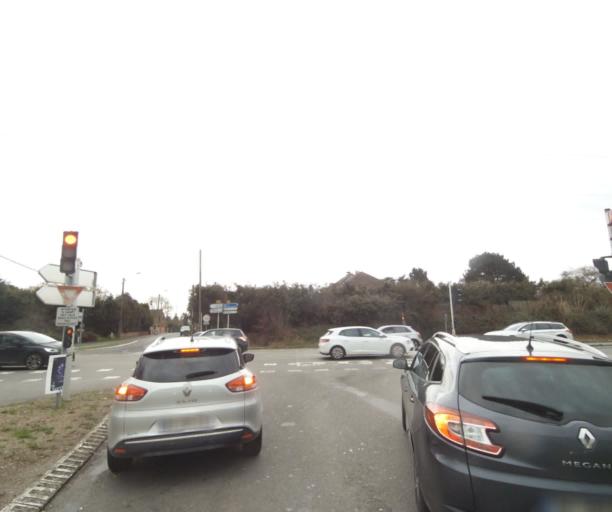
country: FR
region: Nord-Pas-de-Calais
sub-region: Departement du Nord
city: Saint-Saulve
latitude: 50.3613
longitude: 3.5635
